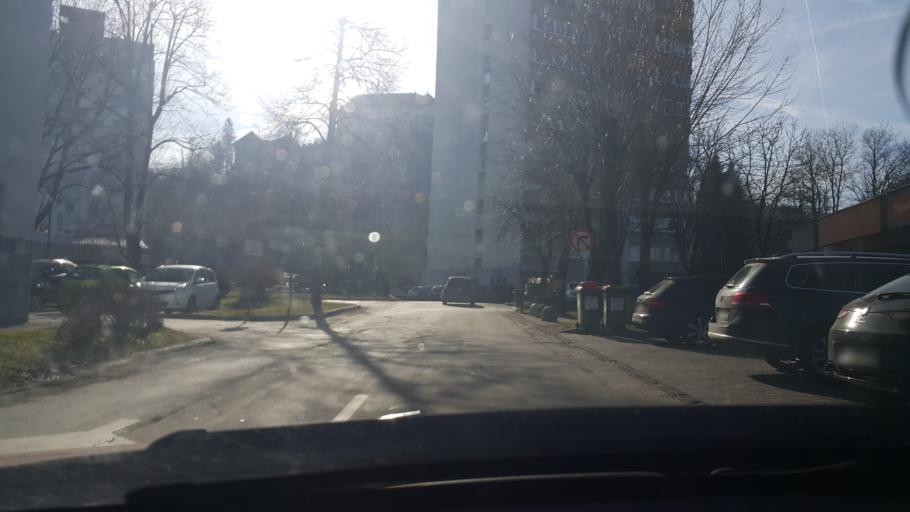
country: SI
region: Velenje
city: Velenje
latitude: 46.3594
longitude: 15.1101
